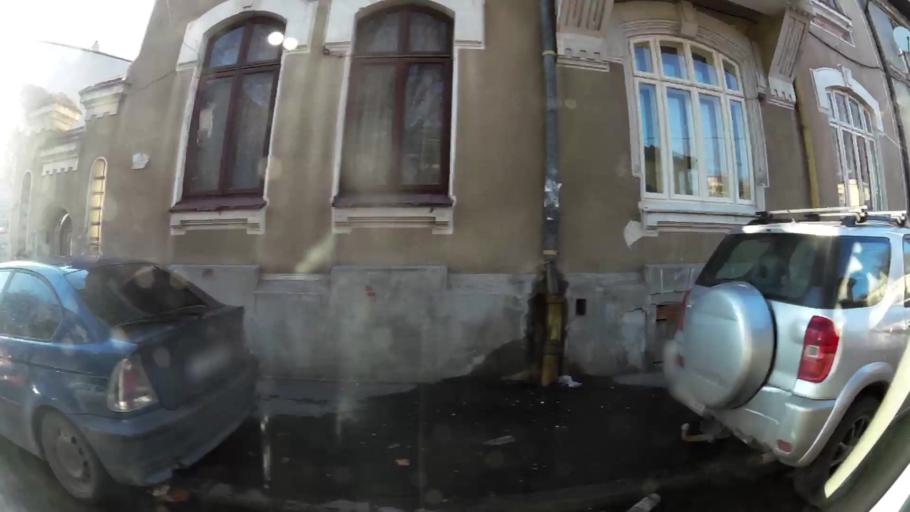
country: RO
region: Bucuresti
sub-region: Municipiul Bucuresti
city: Bucharest
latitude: 44.4438
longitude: 26.1136
